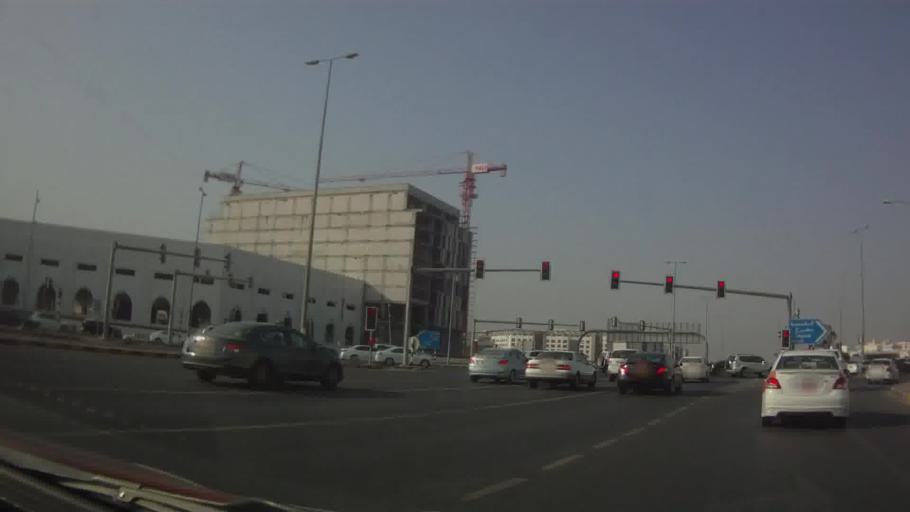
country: OM
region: Muhafazat Masqat
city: Bawshar
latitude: 23.5881
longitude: 58.4135
